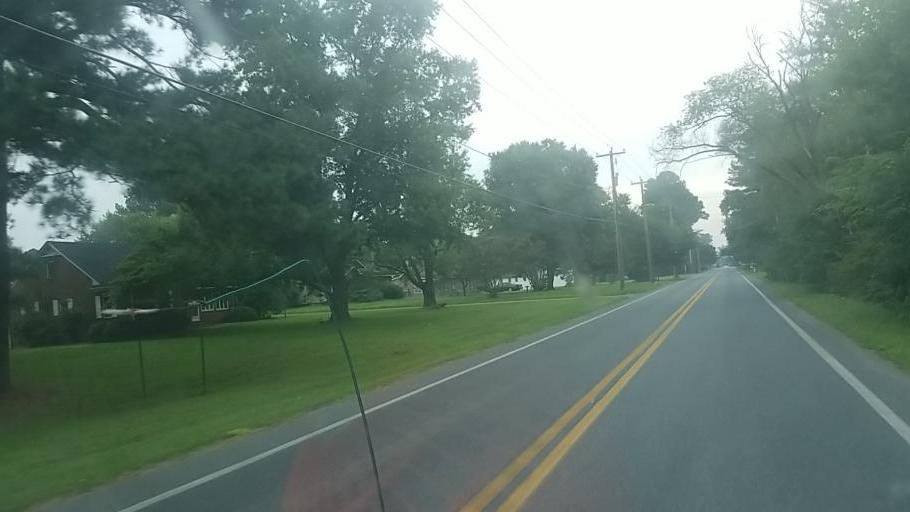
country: US
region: Maryland
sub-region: Wicomico County
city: Salisbury
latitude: 38.3764
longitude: -75.5289
